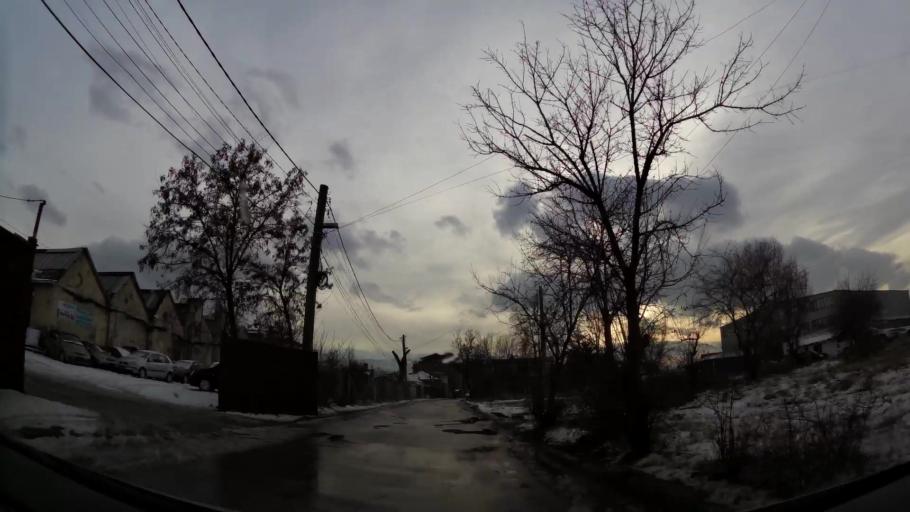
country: BG
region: Sofia-Capital
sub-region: Stolichna Obshtina
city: Sofia
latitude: 42.7228
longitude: 23.3366
